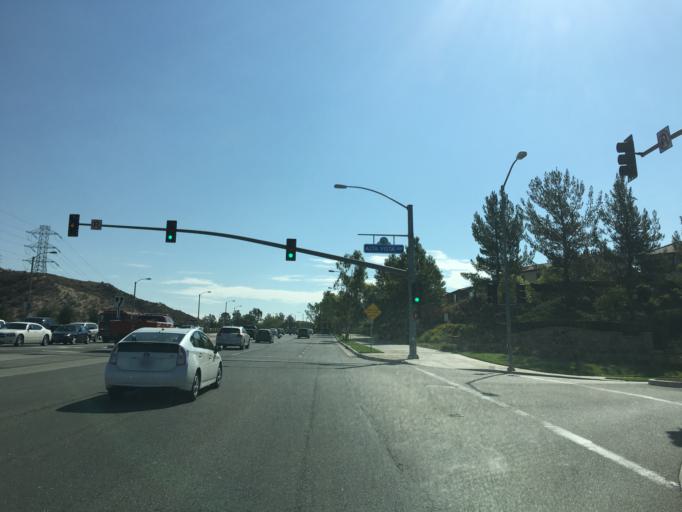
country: US
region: California
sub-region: Los Angeles County
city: Valencia
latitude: 34.4464
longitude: -118.5714
